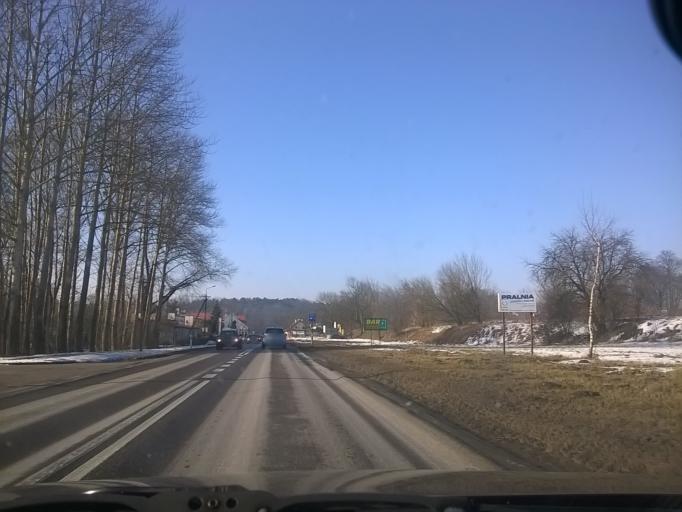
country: PL
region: Warmian-Masurian Voivodeship
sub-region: Powiat mragowski
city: Mragowo
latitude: 53.8444
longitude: 21.1480
